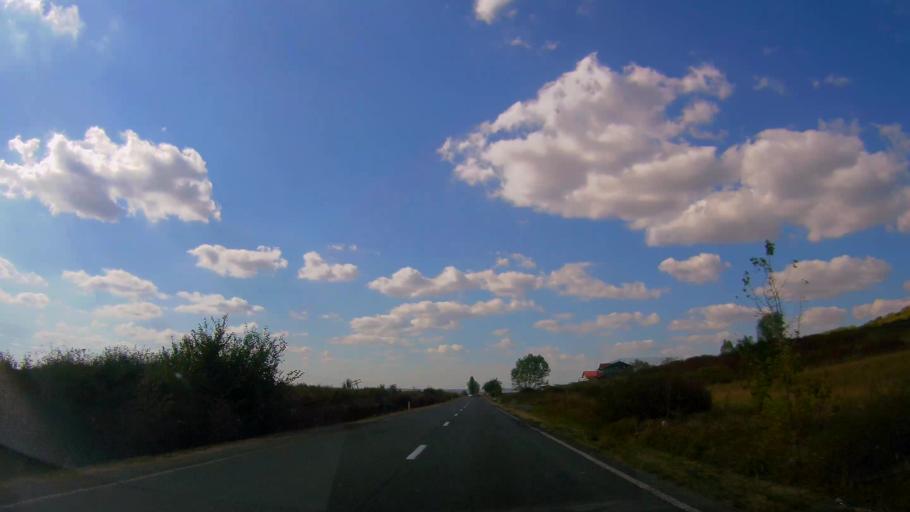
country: RO
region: Salaj
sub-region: Comuna Sarmasag
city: Sarmasag
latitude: 47.3297
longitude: 22.8628
